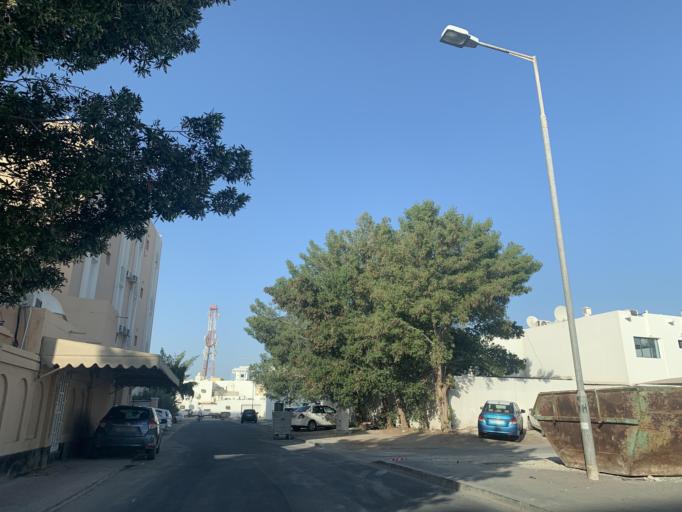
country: BH
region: Manama
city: Manama
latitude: 26.2014
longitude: 50.5878
